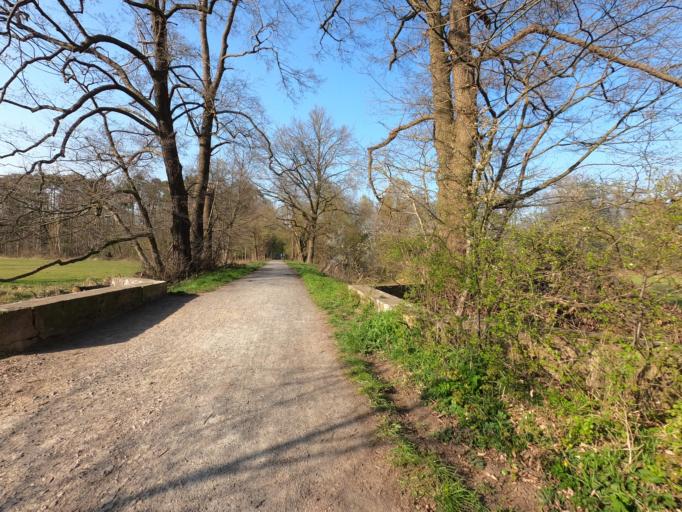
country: DE
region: Hesse
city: Morfelden-Walldorf
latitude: 49.9706
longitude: 8.5409
